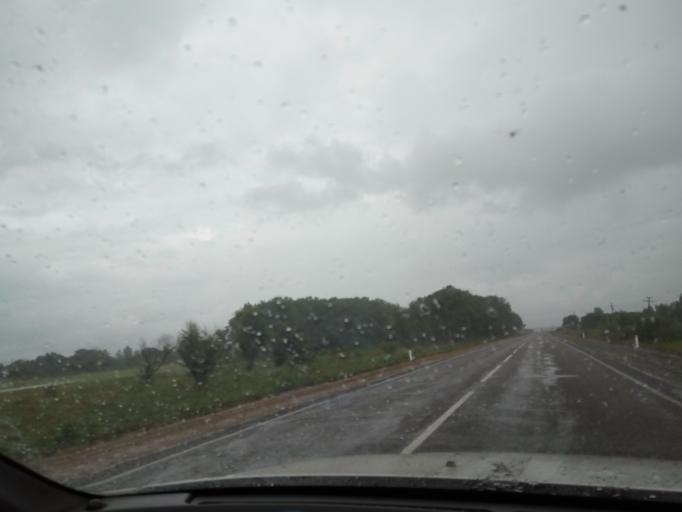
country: RU
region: Primorskiy
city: Dal'nerechensk
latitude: 45.9045
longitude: 133.7516
